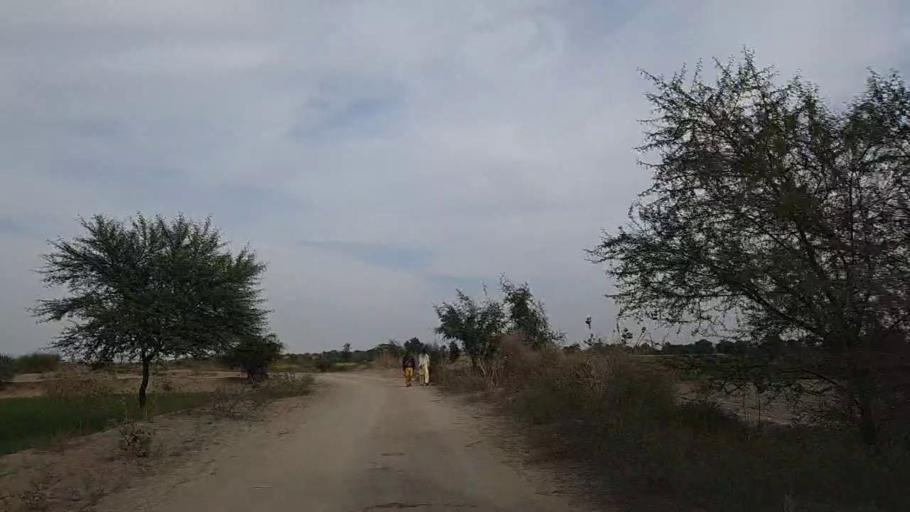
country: PK
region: Sindh
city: Jam Sahib
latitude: 26.4406
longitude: 68.5961
